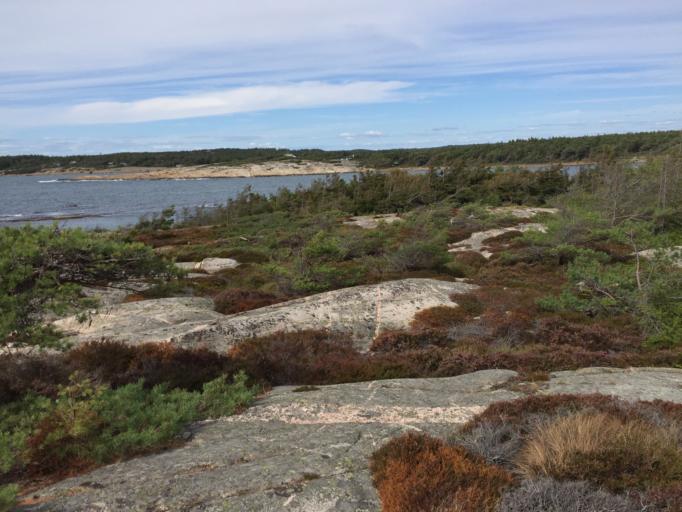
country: NO
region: Ostfold
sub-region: Hvaler
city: Skjaerhalden
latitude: 59.0209
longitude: 11.0144
